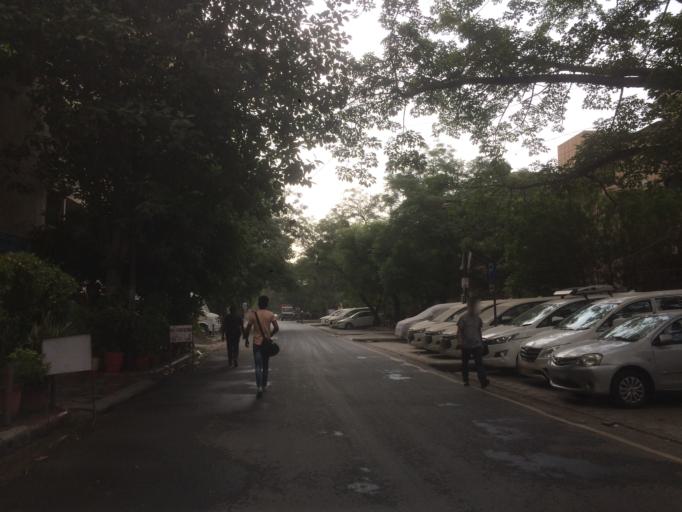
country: IN
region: NCT
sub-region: New Delhi
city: New Delhi
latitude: 28.5673
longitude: 77.1867
